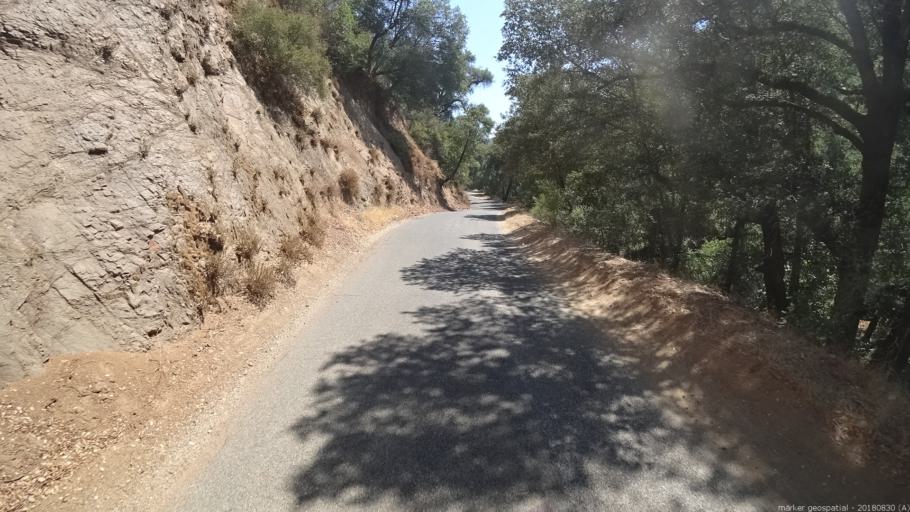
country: US
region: California
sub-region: Monterey County
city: King City
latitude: 36.0118
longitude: -121.4090
